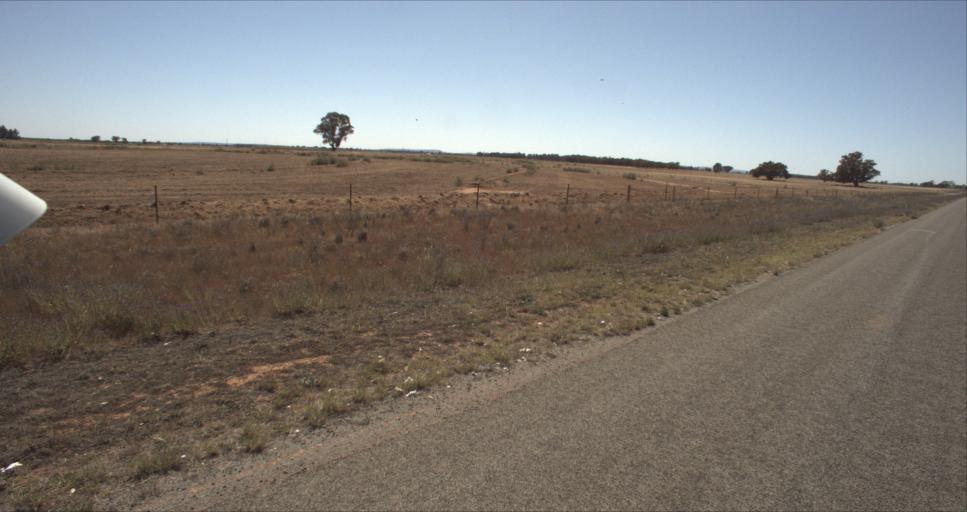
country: AU
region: New South Wales
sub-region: Leeton
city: Leeton
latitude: -34.5814
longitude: 146.2925
